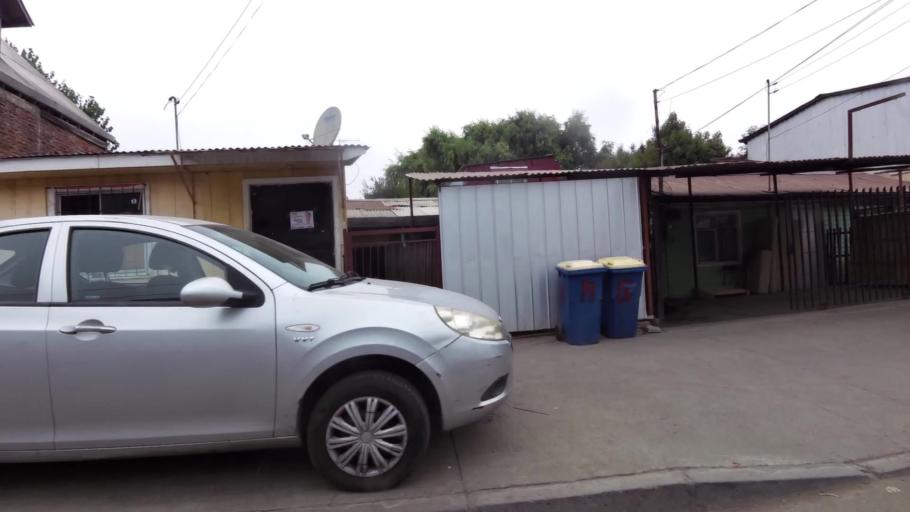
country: CL
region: Biobio
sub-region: Provincia de Concepcion
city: Concepcion
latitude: -36.8397
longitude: -73.0581
